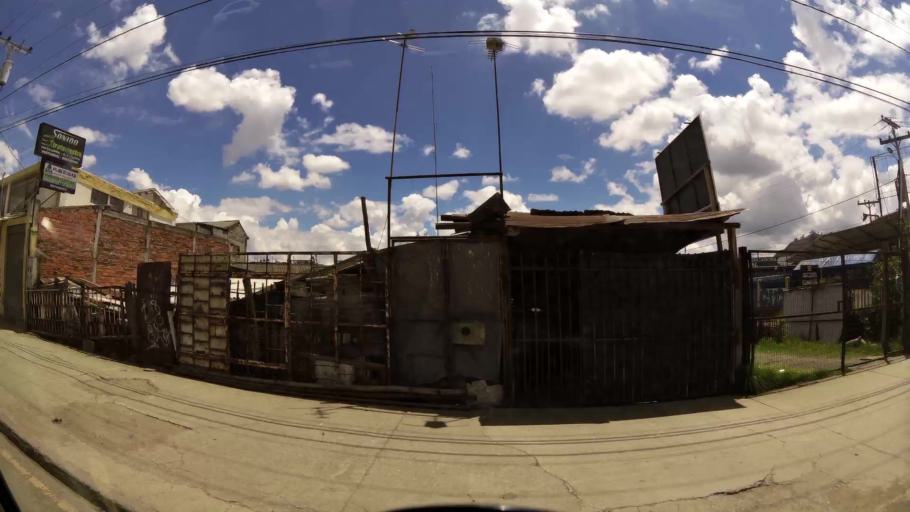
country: EC
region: Azuay
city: Cuenca
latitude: -2.9188
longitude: -79.0389
